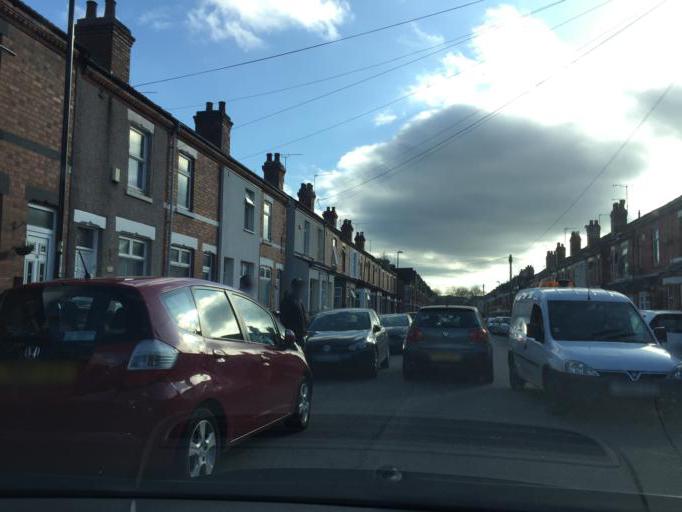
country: GB
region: England
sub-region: Coventry
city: Coventry
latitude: 52.4146
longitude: -1.4933
